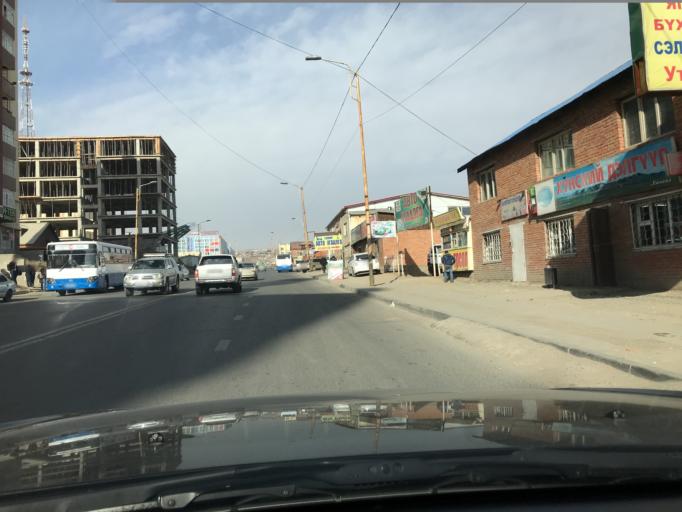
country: MN
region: Ulaanbaatar
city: Ulaanbaatar
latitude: 47.9264
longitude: 106.8943
